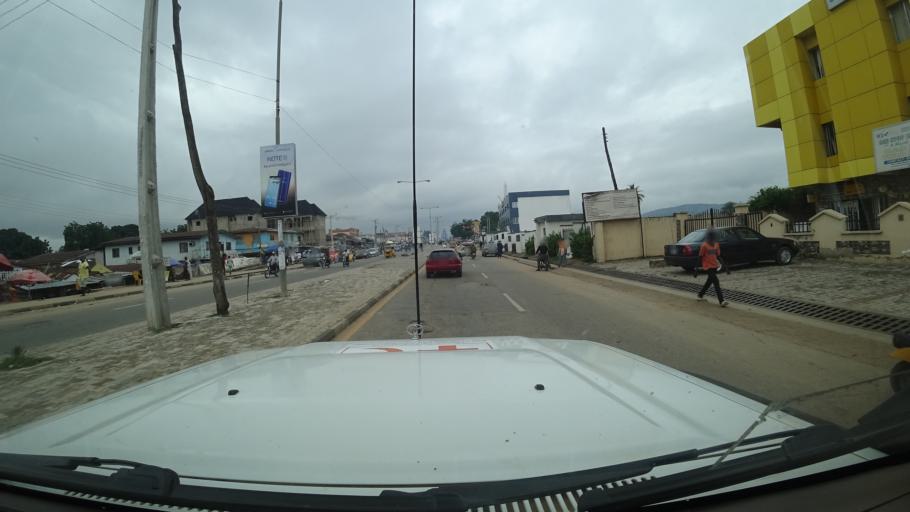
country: NG
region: Niger
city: Minna
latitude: 9.6159
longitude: 6.5470
